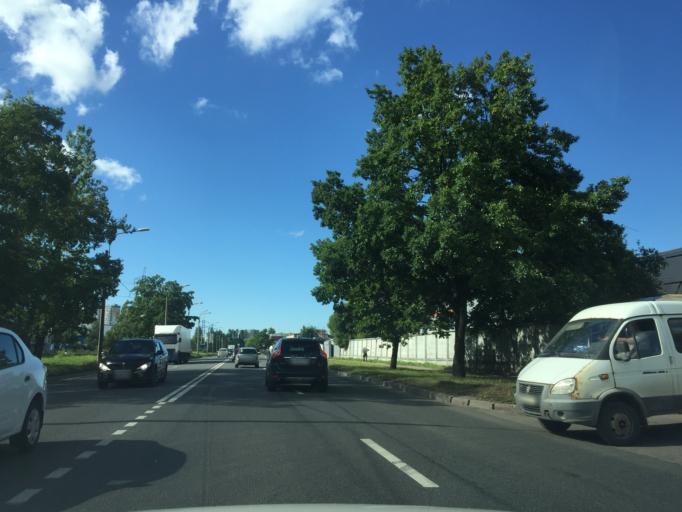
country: RU
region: St.-Petersburg
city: Dachnoye
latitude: 59.8426
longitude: 30.2972
